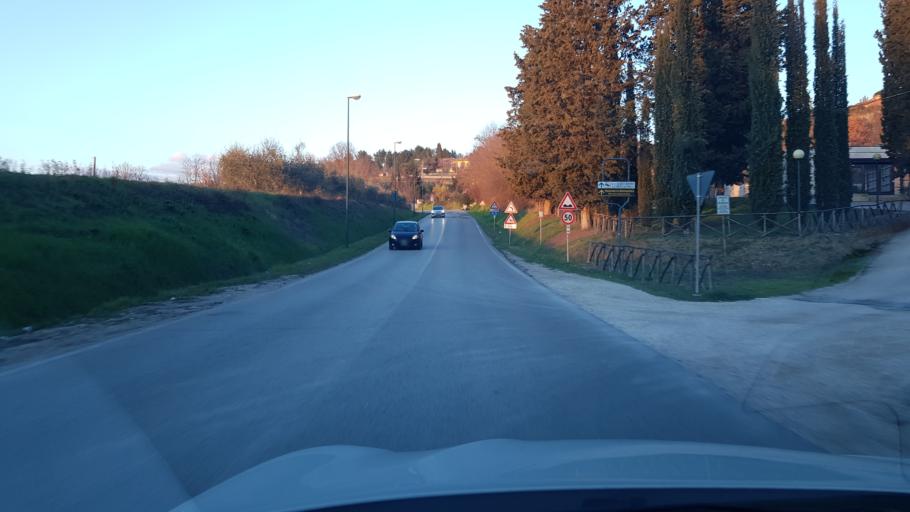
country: IT
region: Umbria
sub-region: Provincia di Perugia
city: Torgiano
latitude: 43.0121
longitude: 12.4349
